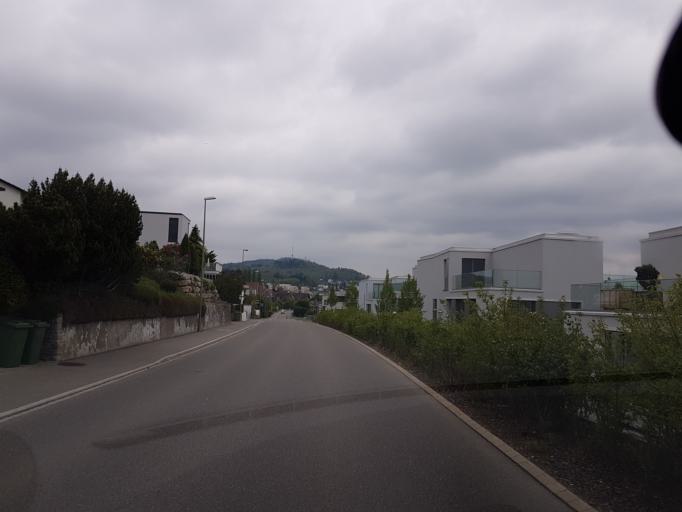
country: CH
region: Zurich
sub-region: Bezirk Dietikon
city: Uitikon
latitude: 47.3740
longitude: 8.4474
